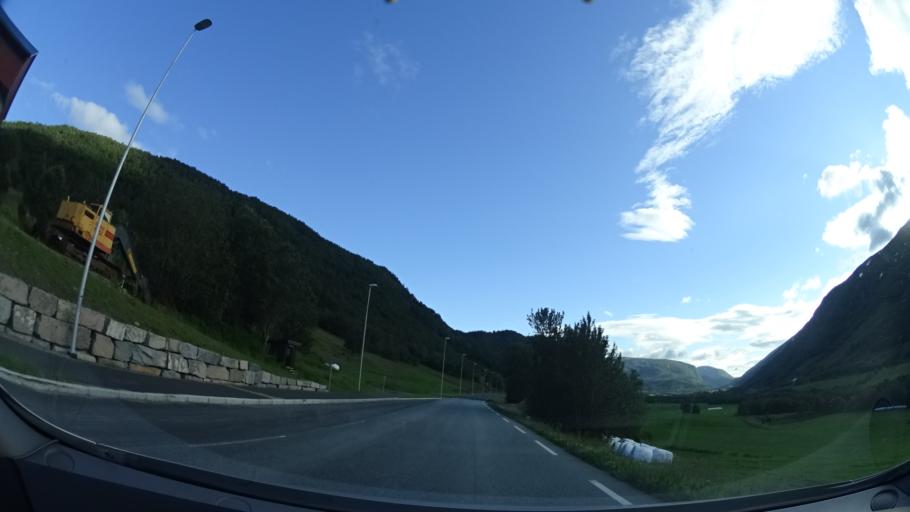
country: NO
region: More og Romsdal
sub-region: Gjemnes
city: Batnfjordsora
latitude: 62.8737
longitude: 7.6379
